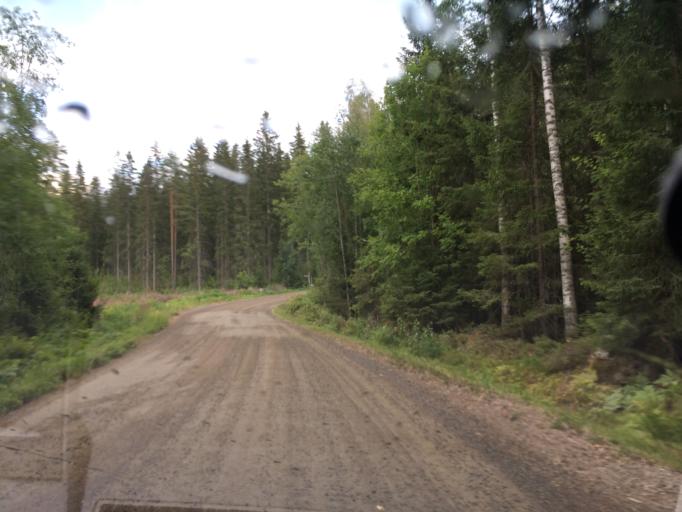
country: FI
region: Pirkanmaa
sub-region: Tampere
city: Luopioinen
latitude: 61.2712
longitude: 24.6755
